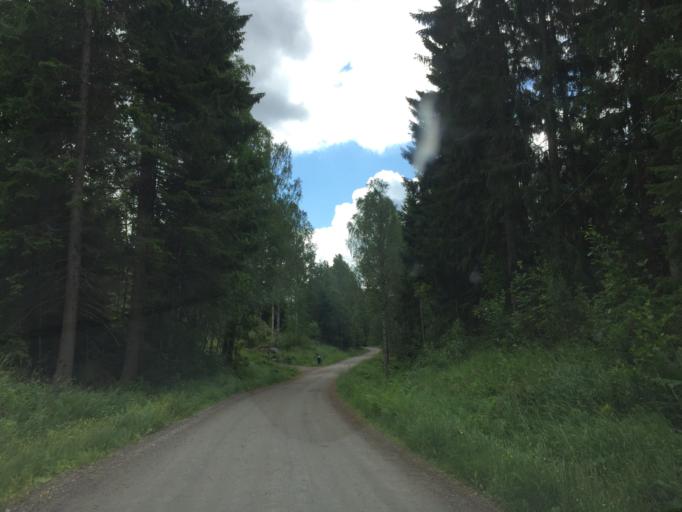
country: SE
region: OErebro
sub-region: Lekebergs Kommun
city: Fjugesta
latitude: 59.2761
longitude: 14.7860
